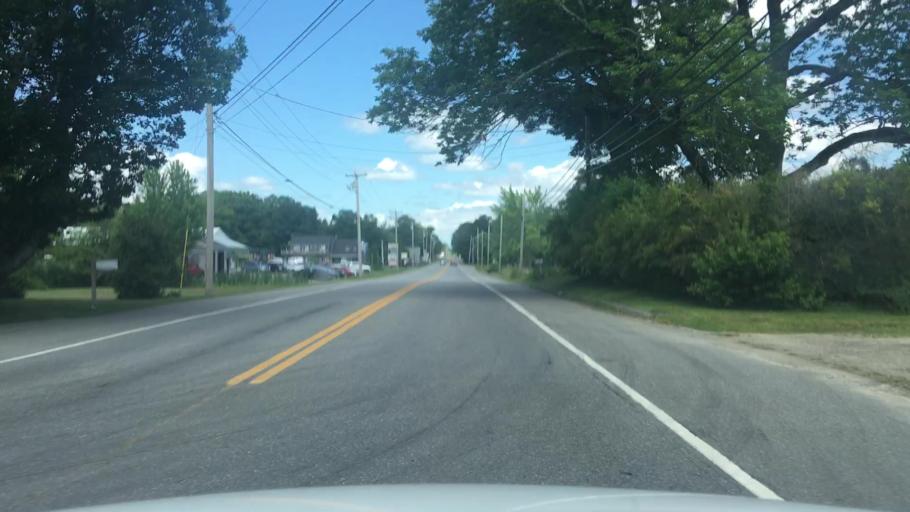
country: US
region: Maine
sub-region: Waldo County
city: Belfast
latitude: 44.4007
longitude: -68.9881
